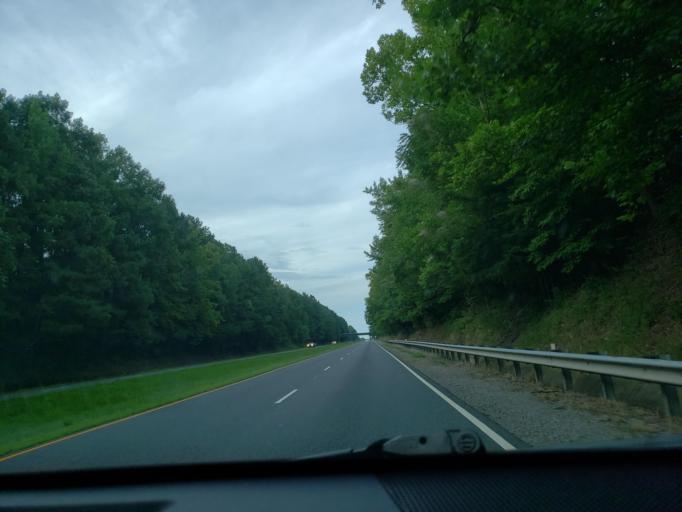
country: US
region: Virginia
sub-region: Brunswick County
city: Lawrenceville
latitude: 36.7538
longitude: -77.8339
